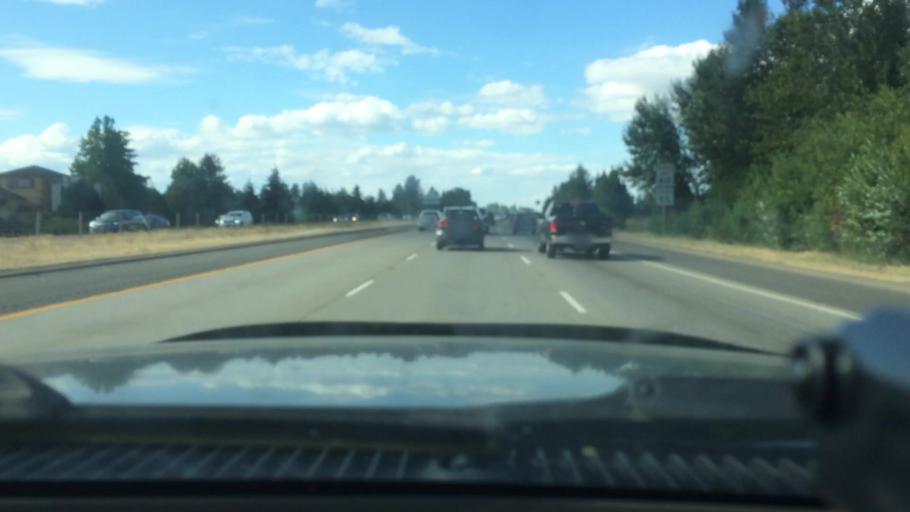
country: US
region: Oregon
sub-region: Marion County
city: Four Corners
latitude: 44.9219
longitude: -122.9900
